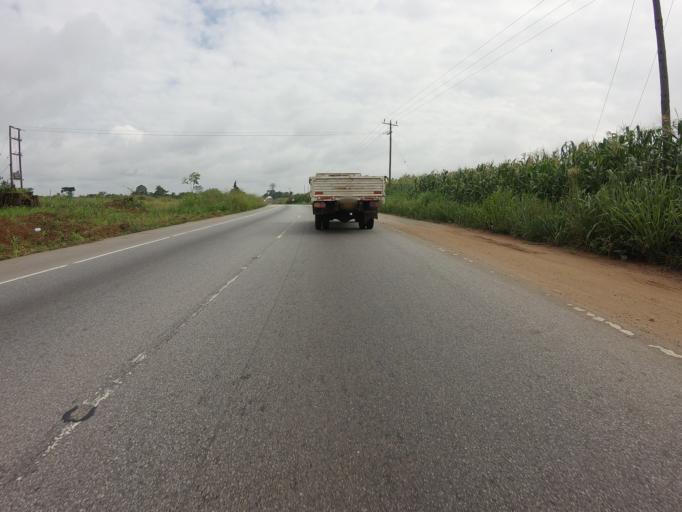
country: GH
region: Ashanti
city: Tafo
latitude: 6.9847
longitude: -1.6884
